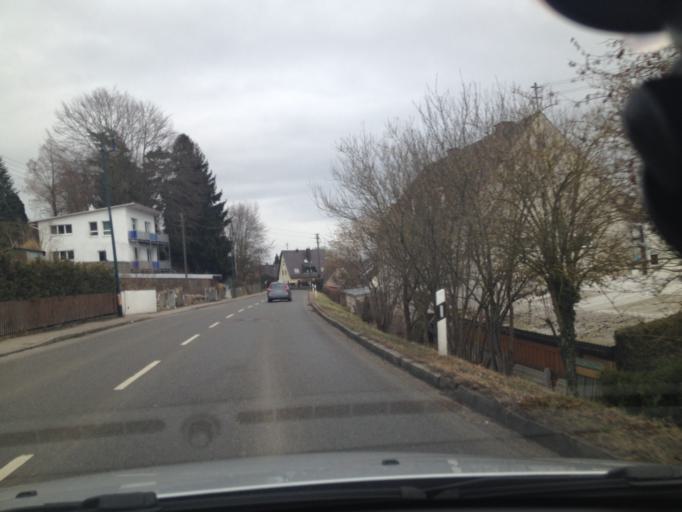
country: DE
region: Bavaria
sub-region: Swabia
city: Aystetten
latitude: 48.4059
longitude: 10.8028
